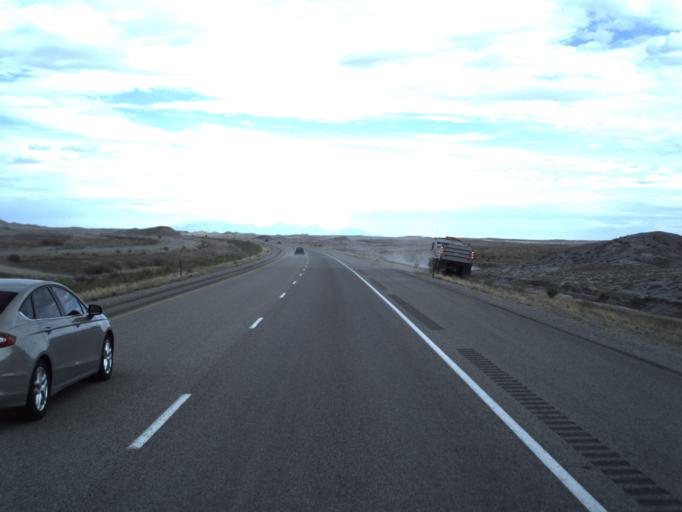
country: US
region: Utah
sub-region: Grand County
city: Moab
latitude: 38.9385
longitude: -110.0314
